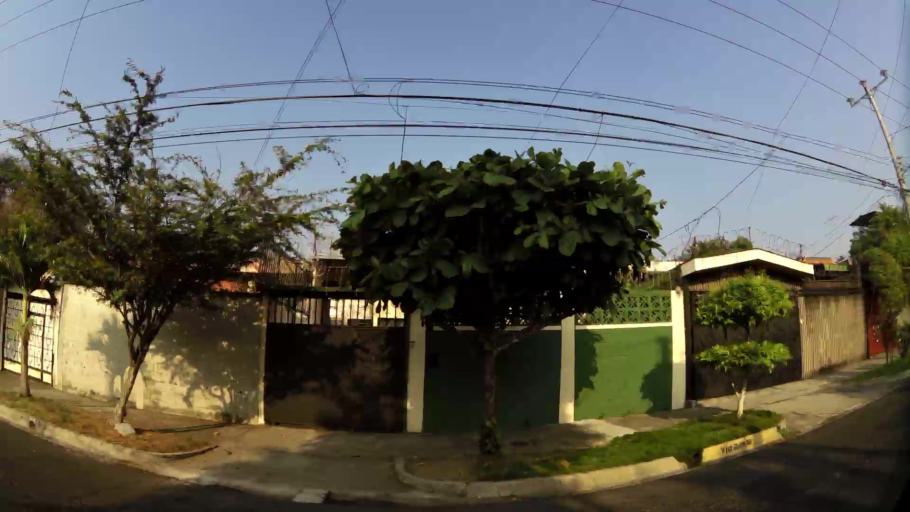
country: SV
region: San Salvador
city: San Salvador
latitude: 13.6770
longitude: -89.2007
